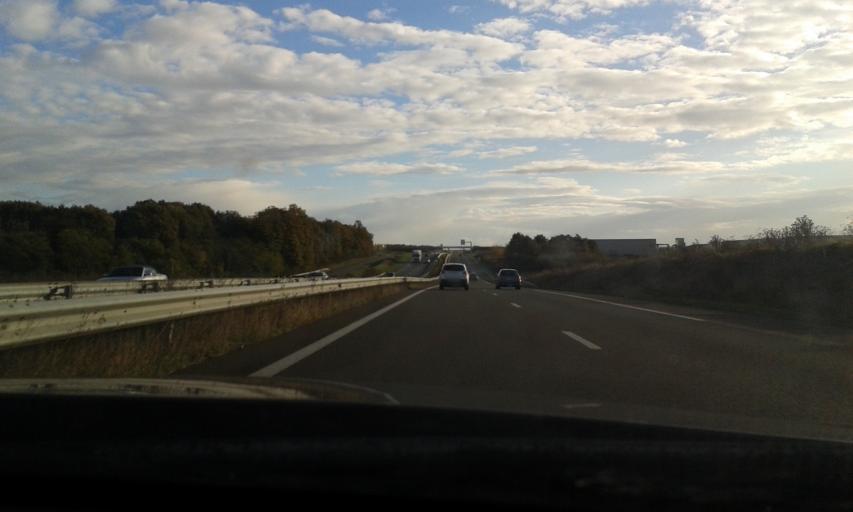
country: FR
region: Centre
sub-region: Departement d'Eure-et-Loir
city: Villemeux-sur-Eure
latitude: 48.6134
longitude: 1.4187
